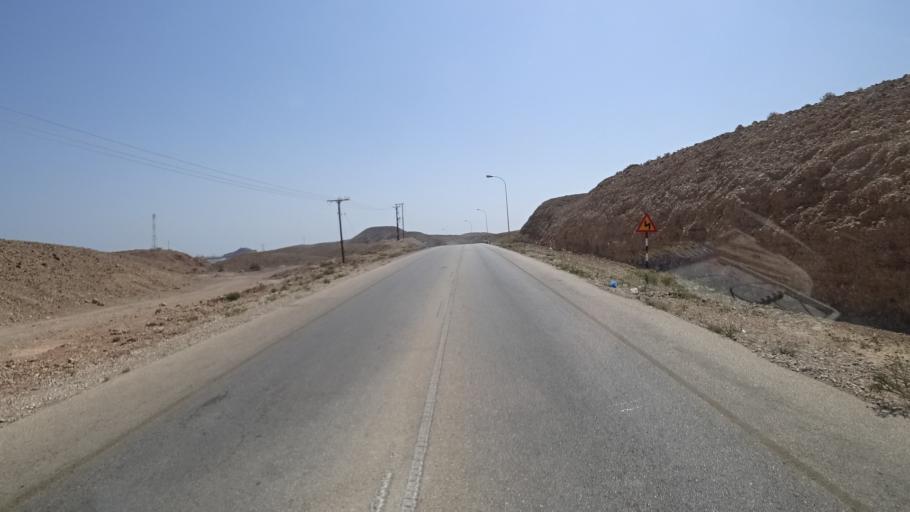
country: OM
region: Ash Sharqiyah
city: Sur
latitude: 22.5448
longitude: 59.5173
